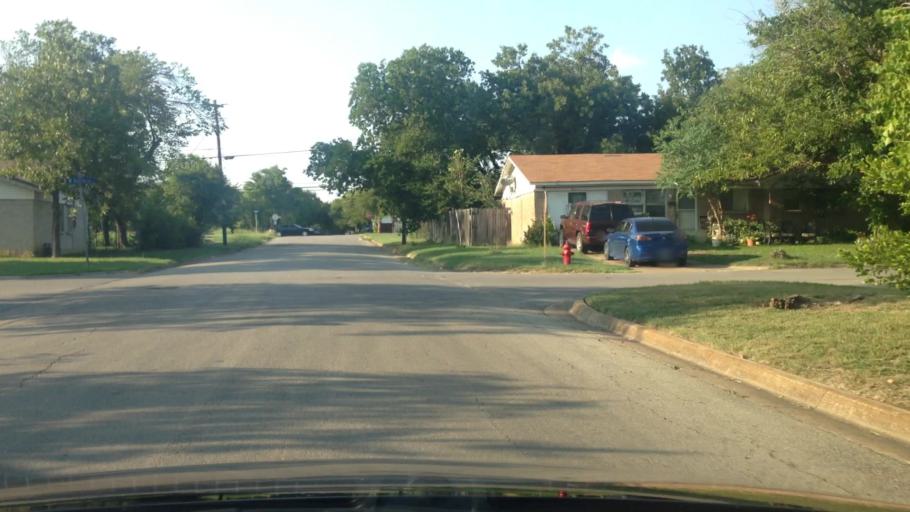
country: US
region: Texas
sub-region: Tarrant County
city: Everman
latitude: 32.6300
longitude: -97.2916
